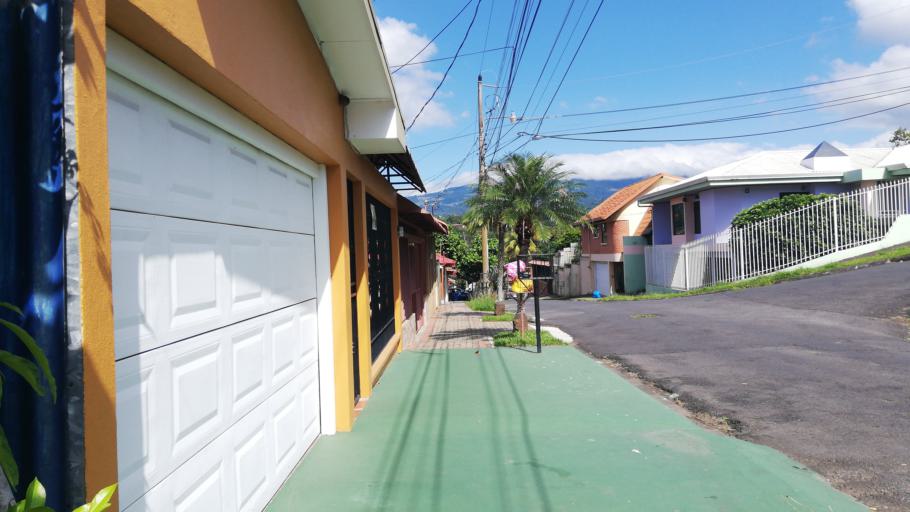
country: CR
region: Alajuela
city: San Juan
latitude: 10.0788
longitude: -84.3110
